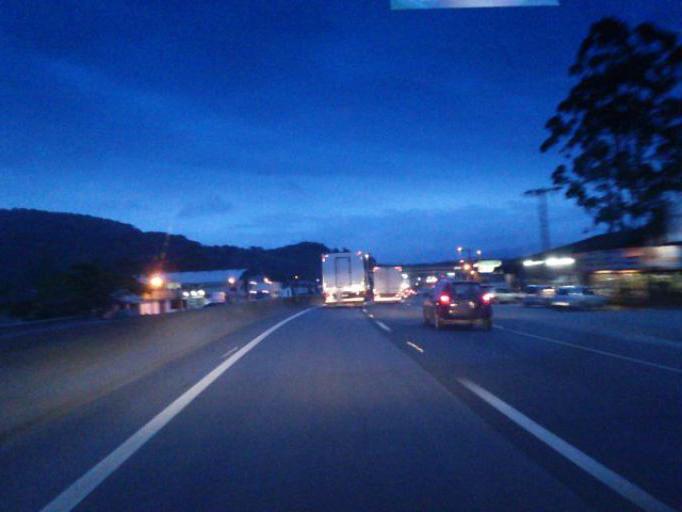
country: BR
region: Santa Catarina
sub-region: Navegantes
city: Navegantes
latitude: -26.8347
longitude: -48.7001
